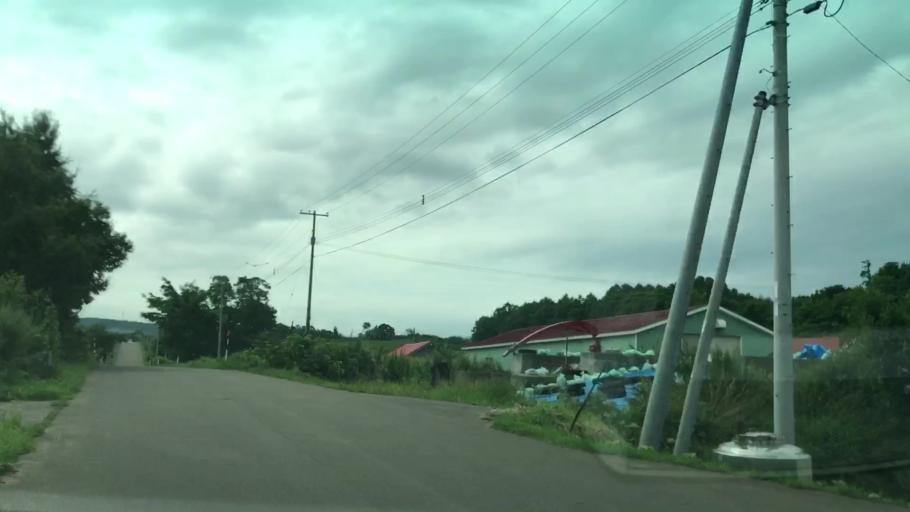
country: JP
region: Hokkaido
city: Yoichi
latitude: 43.1785
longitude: 140.8383
